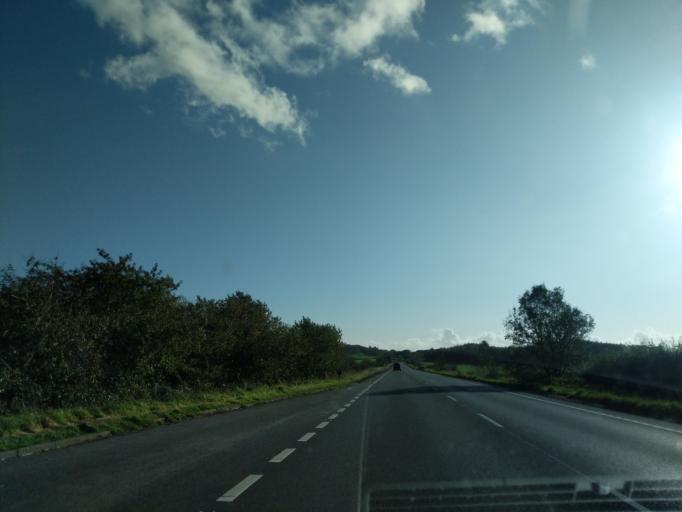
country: GB
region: Scotland
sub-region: Dumfries and Galloway
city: Castle Douglas
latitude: 54.9389
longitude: -3.9469
